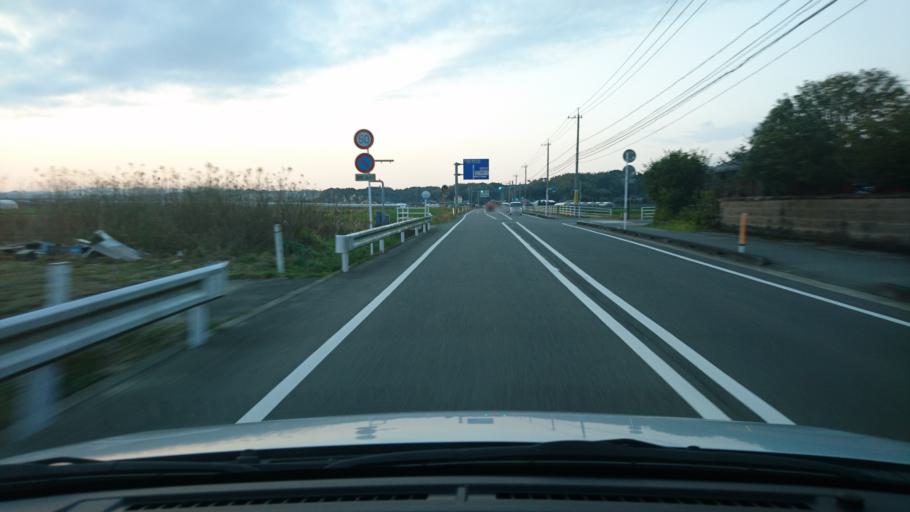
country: JP
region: Miyazaki
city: Miyazaki-shi
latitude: 31.8487
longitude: 131.4226
